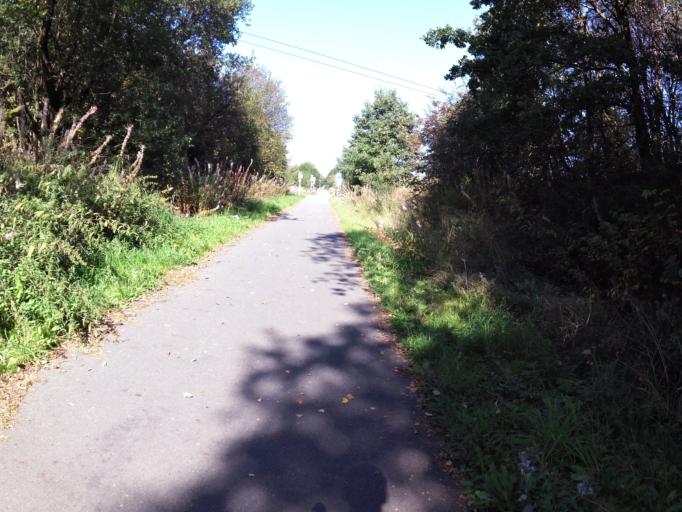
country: BE
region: Wallonia
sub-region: Province de Liege
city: Waimes
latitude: 50.4543
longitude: 6.1477
